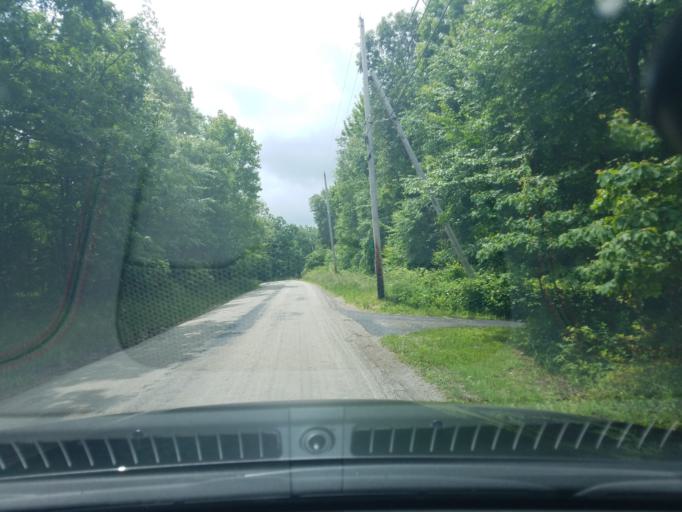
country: US
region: Pennsylvania
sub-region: Fayette County
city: Bear Rocks
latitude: 40.1765
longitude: -79.4110
